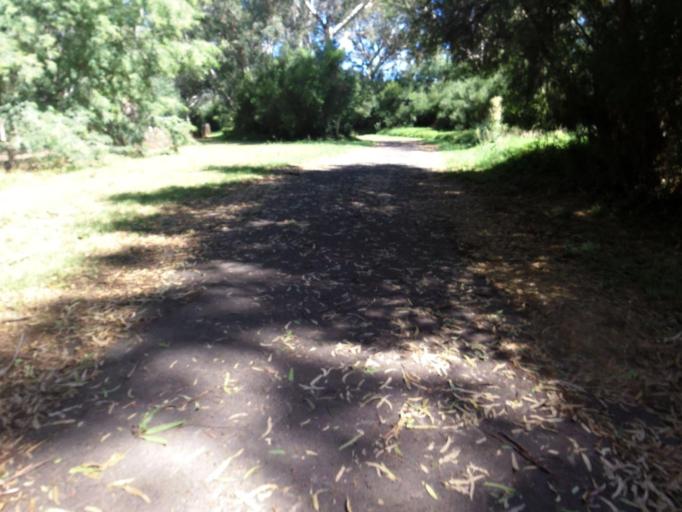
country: AU
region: Victoria
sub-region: Manningham
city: Bulleen
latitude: -37.7544
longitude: 145.0801
